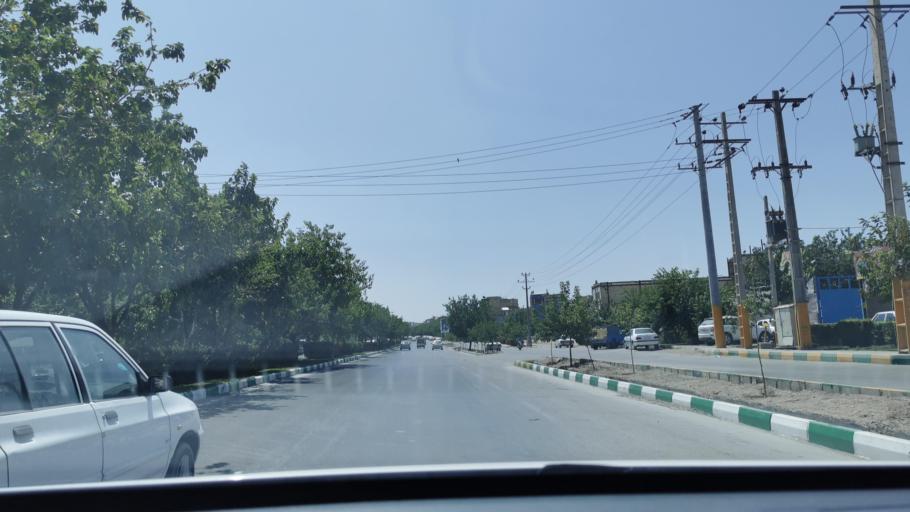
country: IR
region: Razavi Khorasan
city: Mashhad
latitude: 36.3497
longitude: 59.6289
